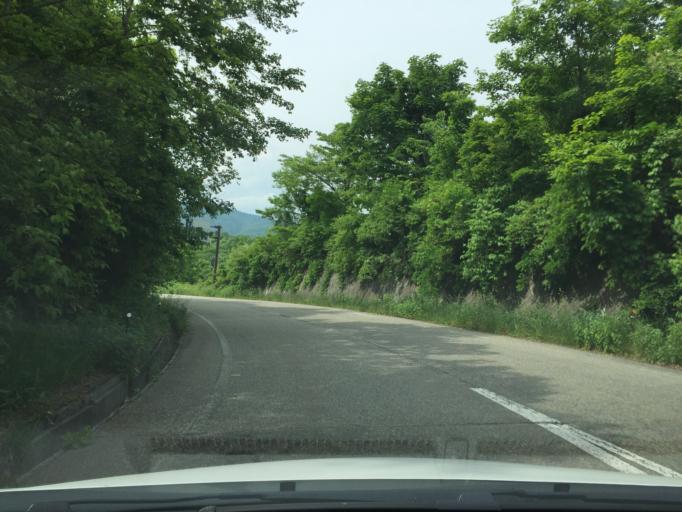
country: JP
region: Fukushima
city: Inawashiro
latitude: 37.6645
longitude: 140.0460
